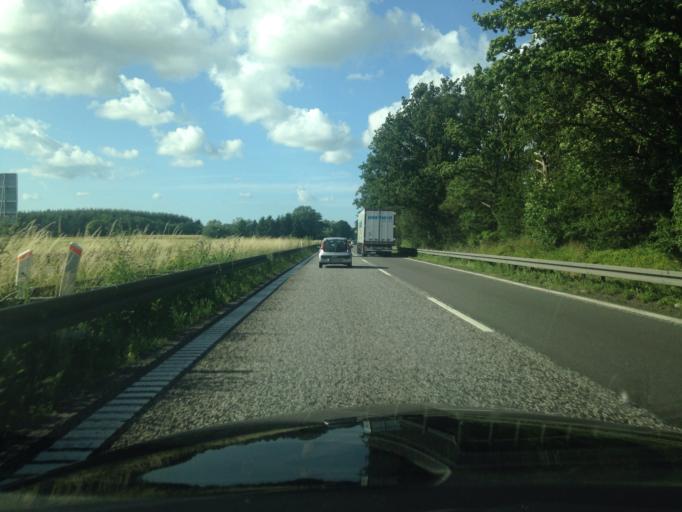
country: DK
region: Capital Region
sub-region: Horsholm Kommune
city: Horsholm
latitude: 55.8815
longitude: 12.4796
